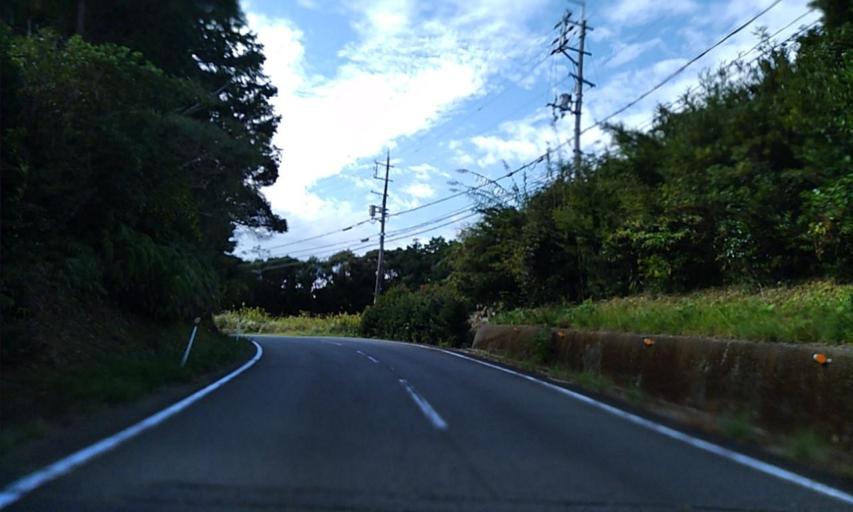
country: JP
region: Wakayama
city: Shingu
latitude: 33.4701
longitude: 135.8454
